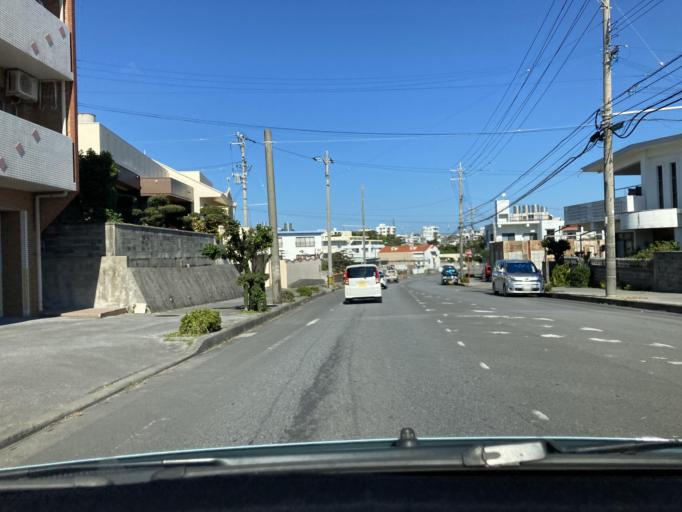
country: JP
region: Okinawa
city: Gushikawa
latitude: 26.3771
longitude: 127.8646
